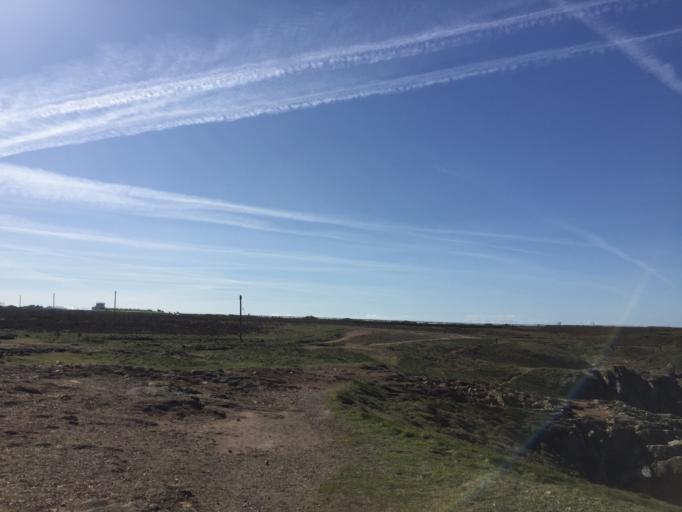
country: JE
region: St Helier
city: Saint Helier
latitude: 49.2571
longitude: -2.2463
